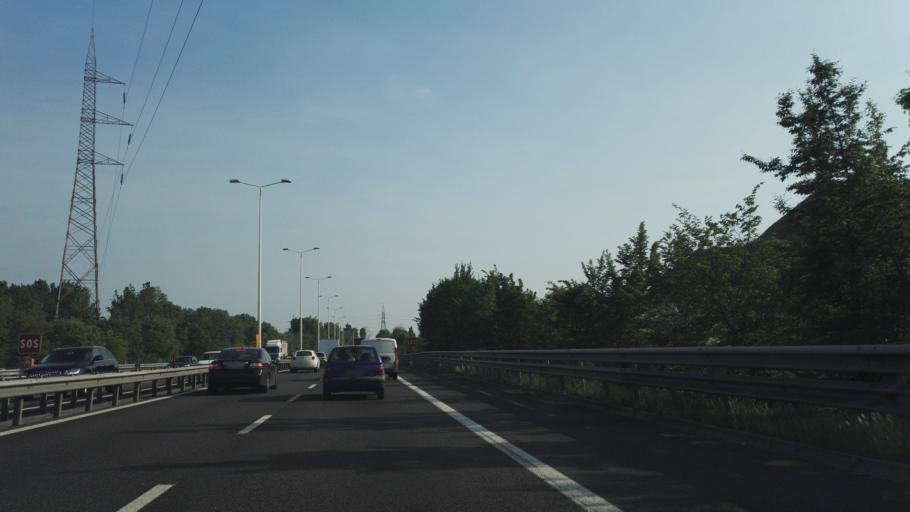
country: IT
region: Lombardy
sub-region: Citta metropolitana di Milano
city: Cologno Monzese
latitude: 45.5363
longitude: 9.2617
